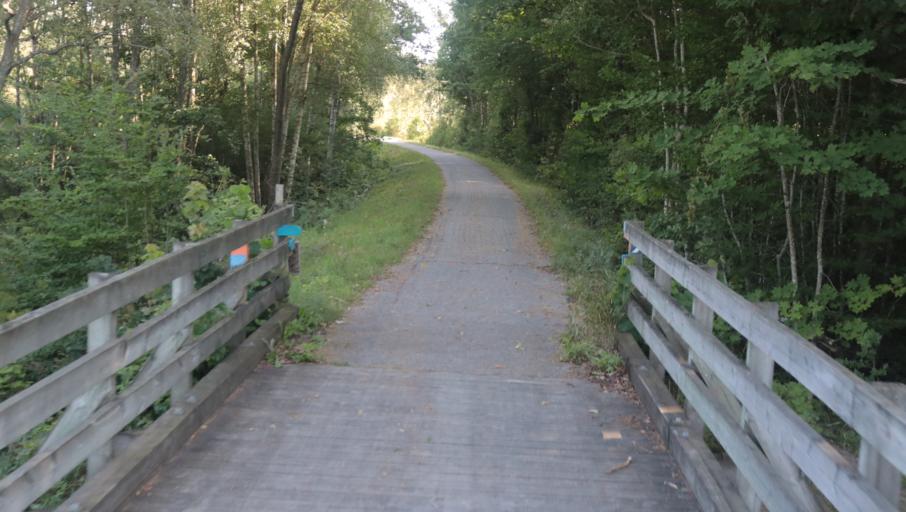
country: SE
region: Blekinge
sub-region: Karlshamns Kommun
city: Svangsta
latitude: 56.3772
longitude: 14.6801
